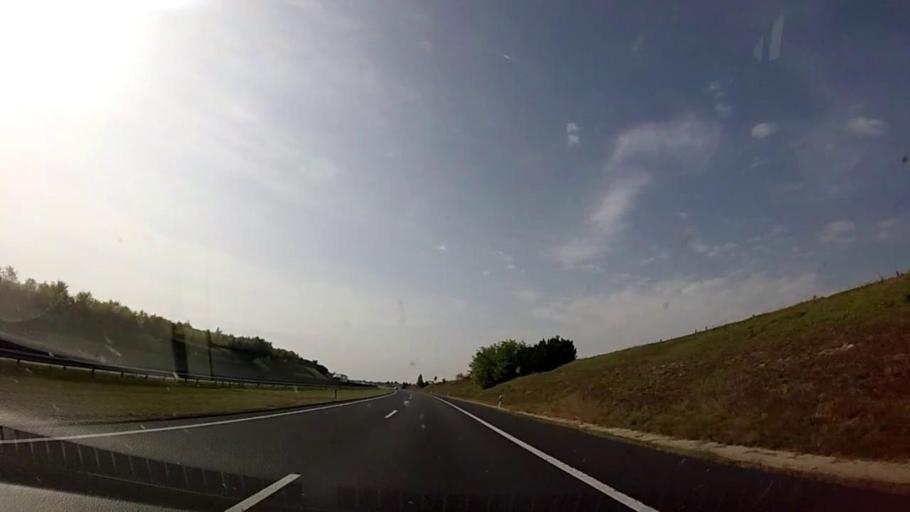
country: HU
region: Zala
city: Nagykanizsa
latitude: 46.4745
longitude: 16.9015
